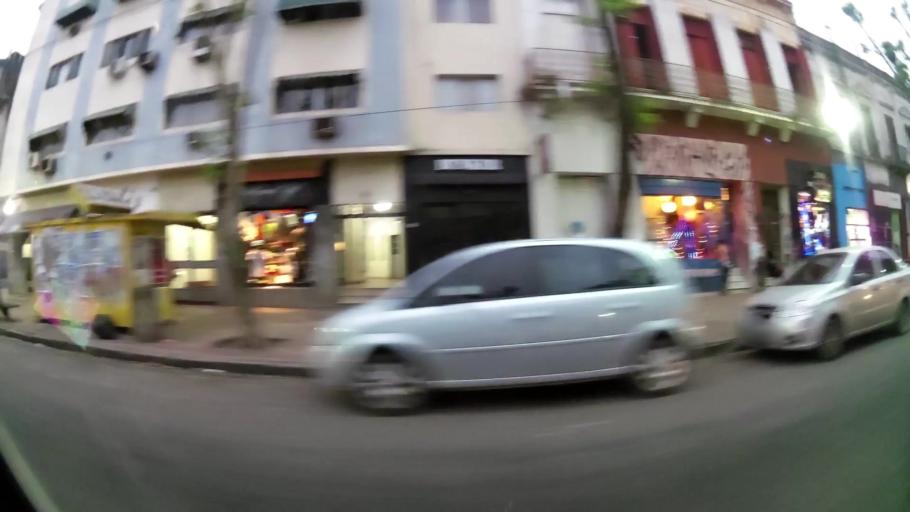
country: AR
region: Buenos Aires
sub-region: Partido de La Plata
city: La Plata
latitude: -34.9130
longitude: -57.9551
